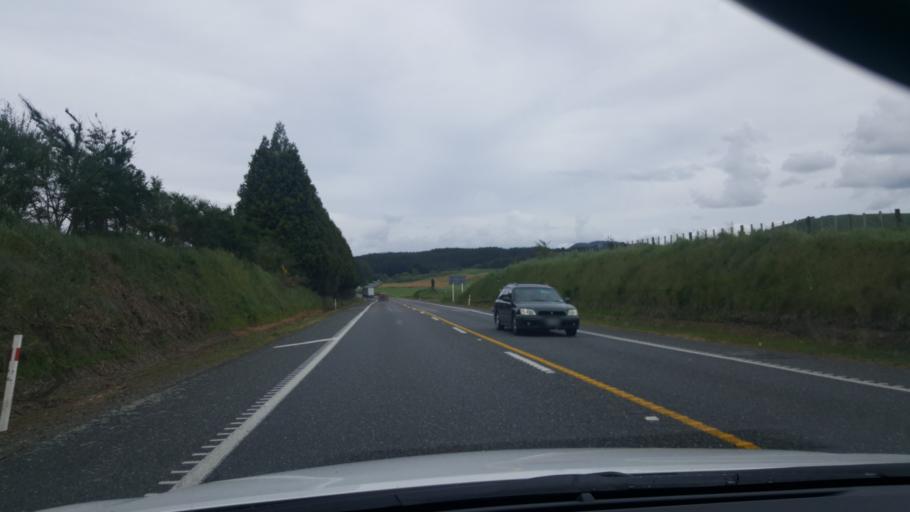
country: NZ
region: Bay of Plenty
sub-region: Rotorua District
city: Rotorua
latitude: -38.2691
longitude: 176.3328
